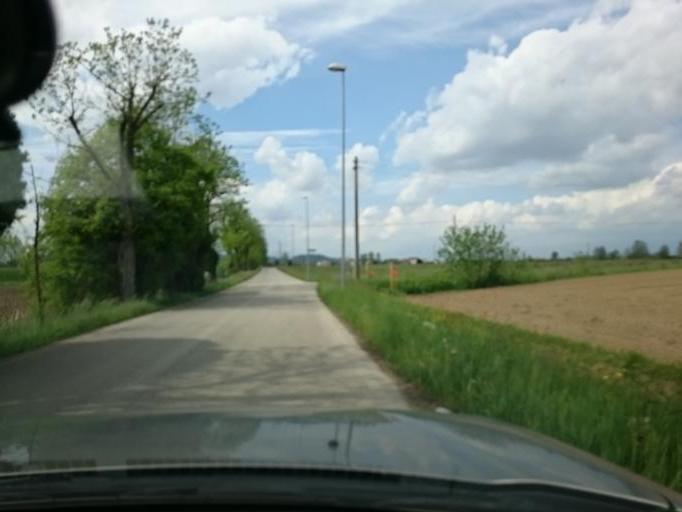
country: IT
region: Veneto
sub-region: Provincia di Vicenza
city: Longare
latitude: 45.4992
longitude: 11.5930
